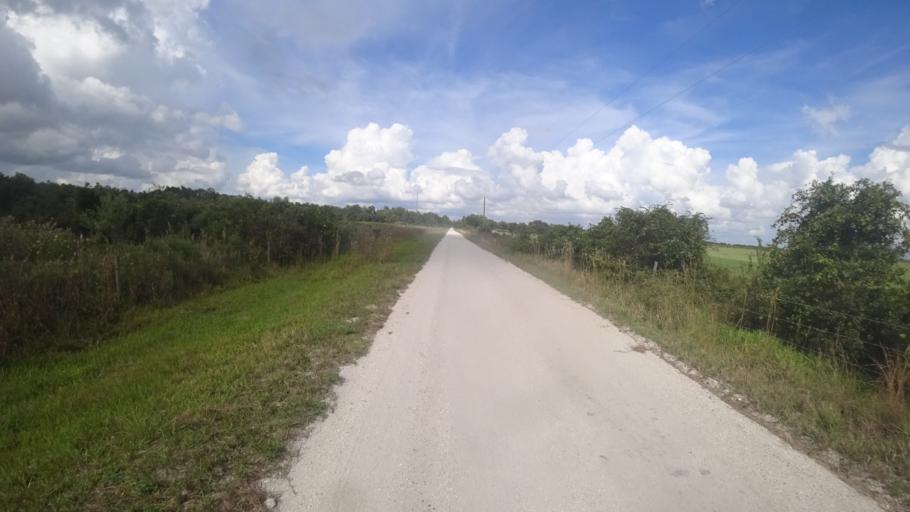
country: US
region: Florida
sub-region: Hillsborough County
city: Wimauma
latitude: 27.5437
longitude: -82.1746
